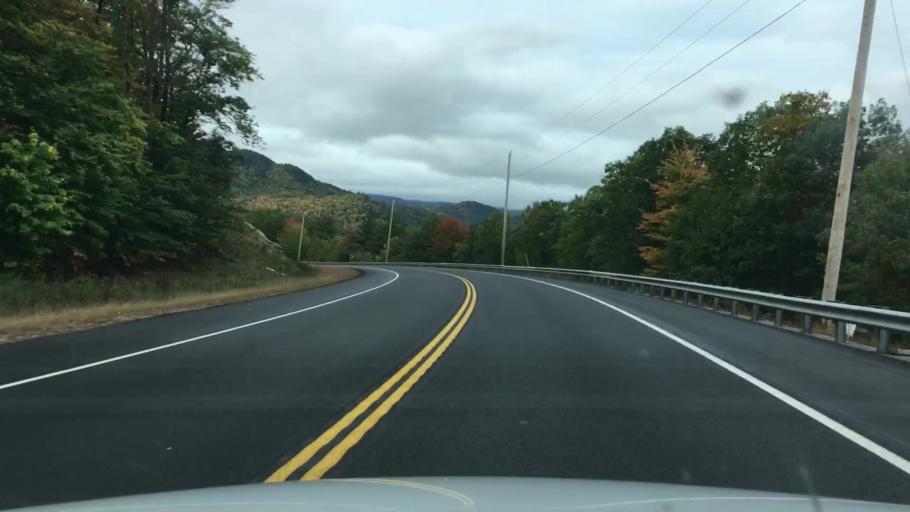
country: US
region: Maine
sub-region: Oxford County
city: Bethel
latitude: 44.4051
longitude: -70.9234
